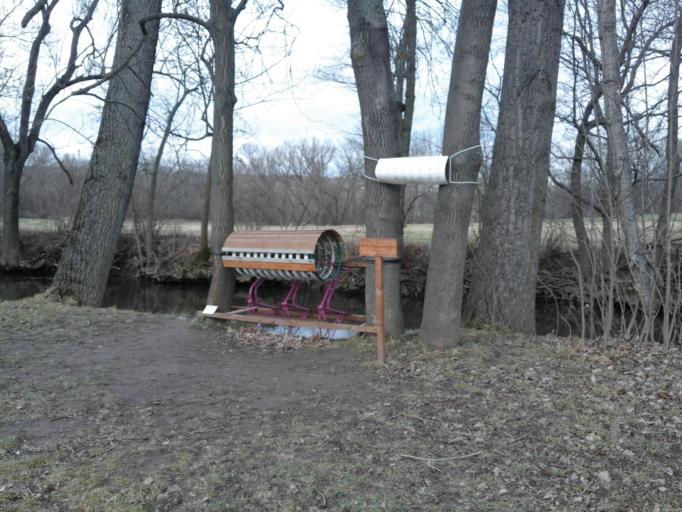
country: DE
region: Thuringia
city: Kromsdorf
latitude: 50.9978
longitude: 11.3592
